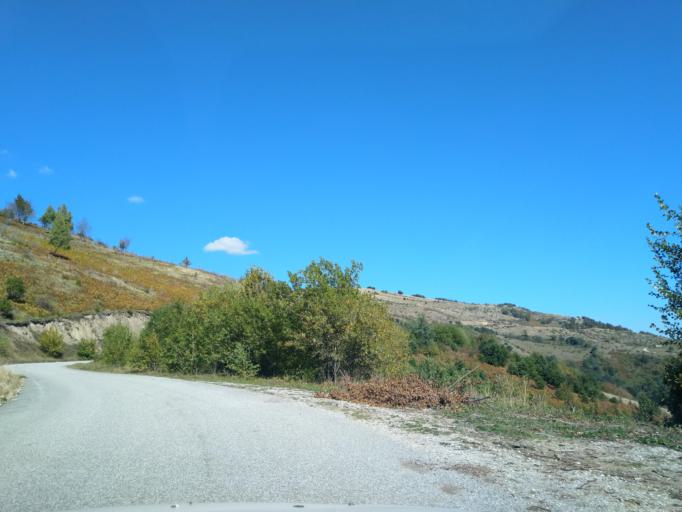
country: RS
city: Sokolovica
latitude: 43.2501
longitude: 20.3290
